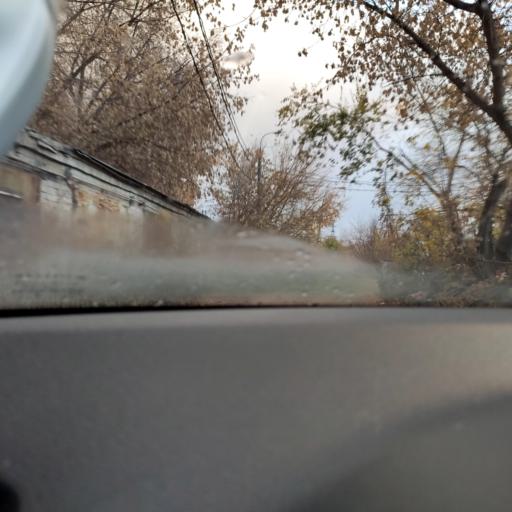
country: RU
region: Samara
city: Smyshlyayevka
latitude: 53.2042
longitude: 50.2861
